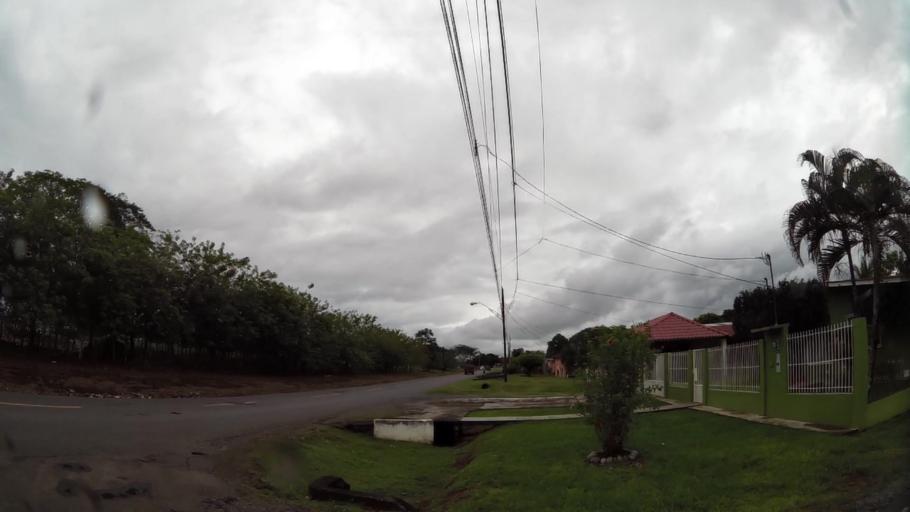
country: PA
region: Chiriqui
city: David
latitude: 8.3988
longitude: -82.4594
